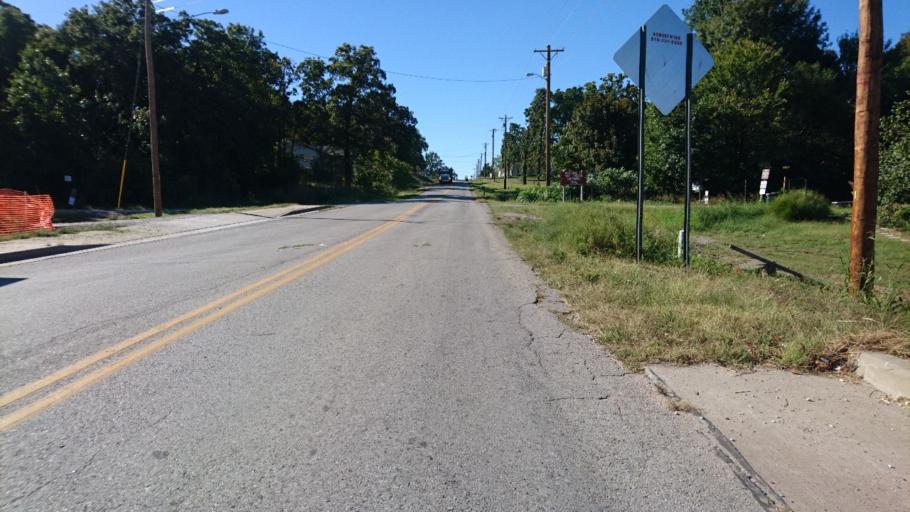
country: US
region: Missouri
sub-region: Jasper County
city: Joplin
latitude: 37.1123
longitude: -94.4941
